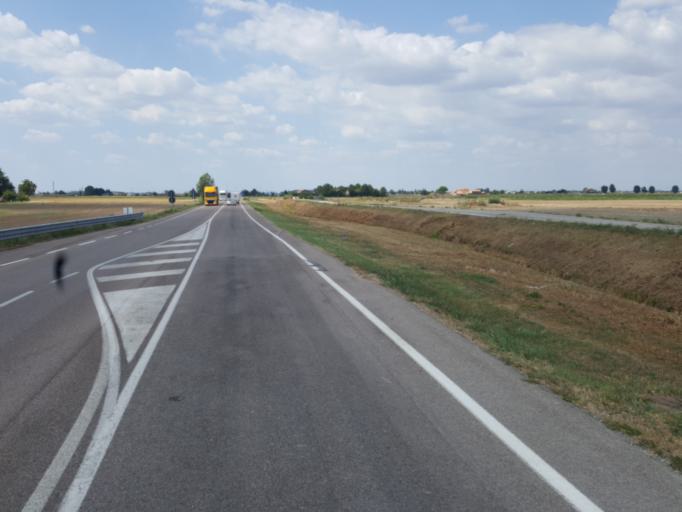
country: IT
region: Veneto
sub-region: Provincia di Rovigo
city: Melara
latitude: 45.0746
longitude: 11.2255
